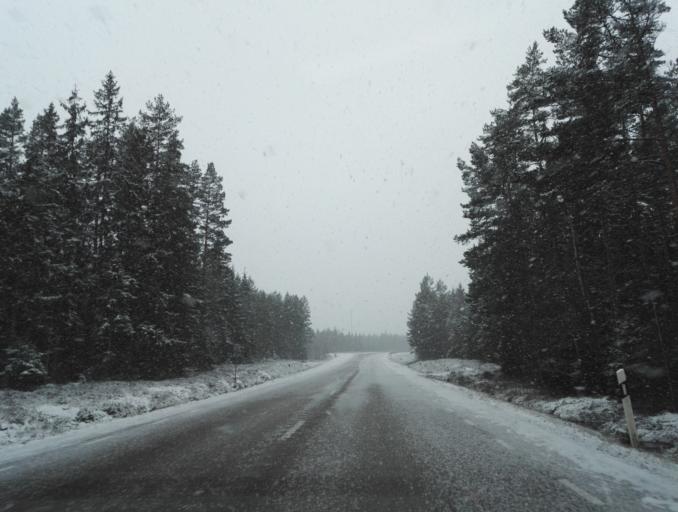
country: SE
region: Kronoberg
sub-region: Uppvidinge Kommun
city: Lenhovda
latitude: 57.0915
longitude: 15.1926
